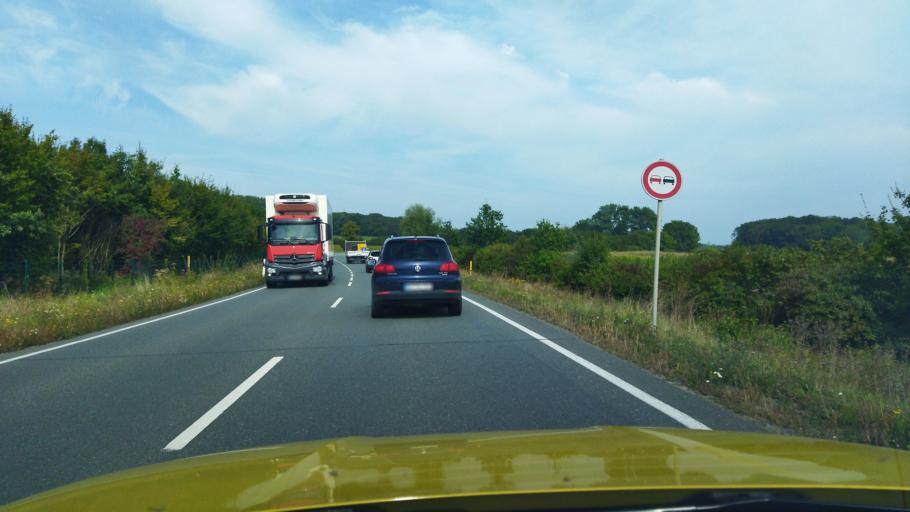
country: DE
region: North Rhine-Westphalia
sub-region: Regierungsbezirk Munster
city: Ennigerloh
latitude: 51.8678
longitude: 8.0304
